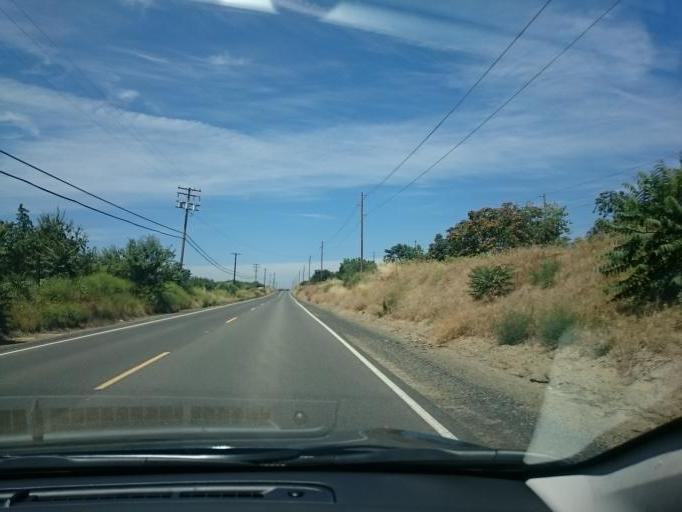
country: US
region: California
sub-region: Stanislaus County
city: Waterford
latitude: 37.6448
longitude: -120.6556
